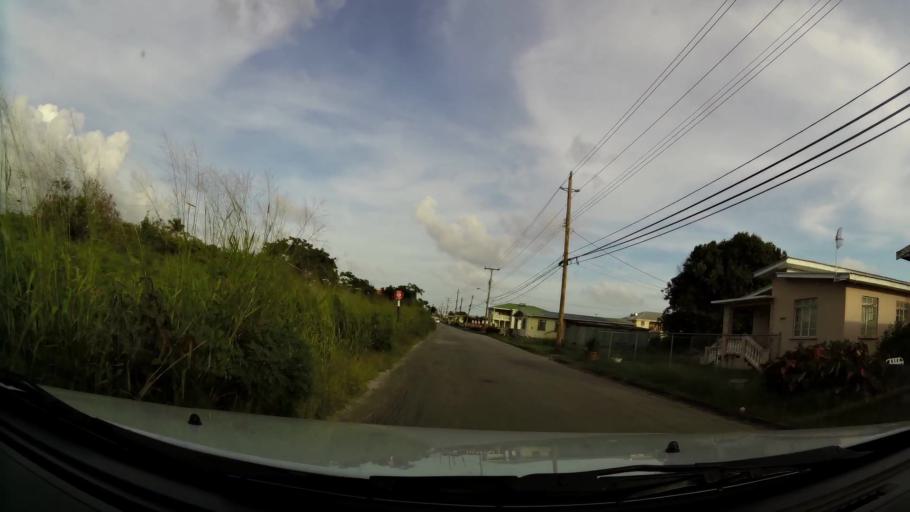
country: BB
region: Christ Church
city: Oistins
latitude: 13.0579
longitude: -59.5199
